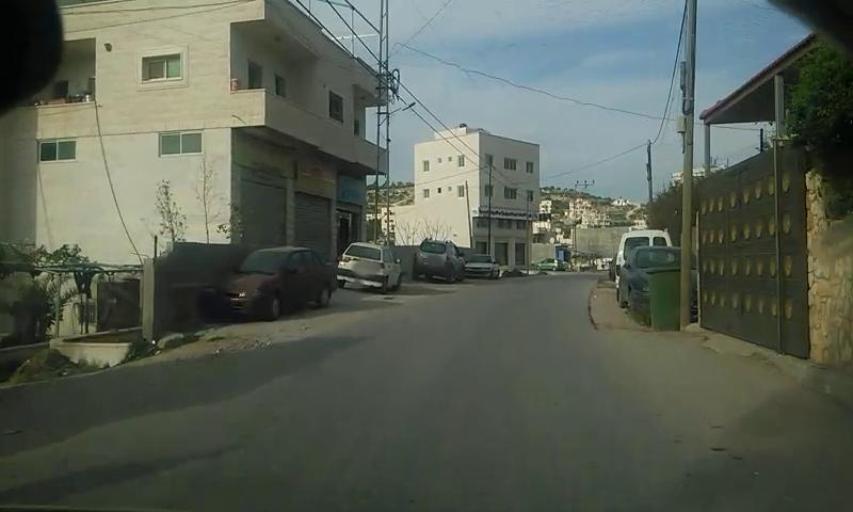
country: PS
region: West Bank
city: Tarqumya
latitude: 31.5797
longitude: 35.0178
